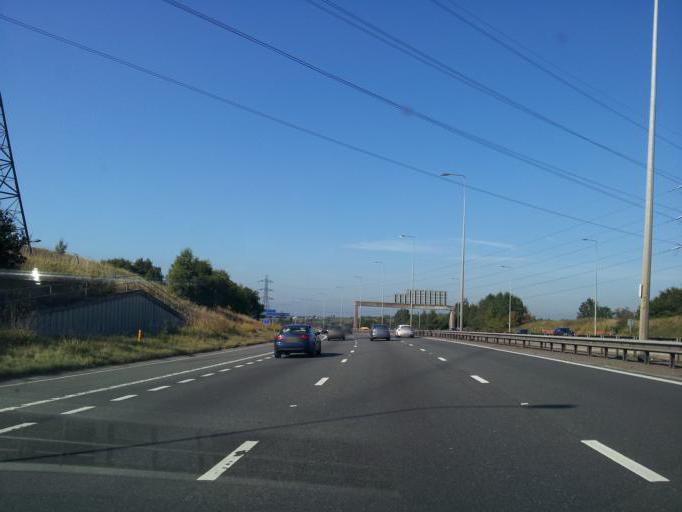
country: GB
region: England
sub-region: Borough of Rochdale
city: Middleton
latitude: 53.5399
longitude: -2.2144
